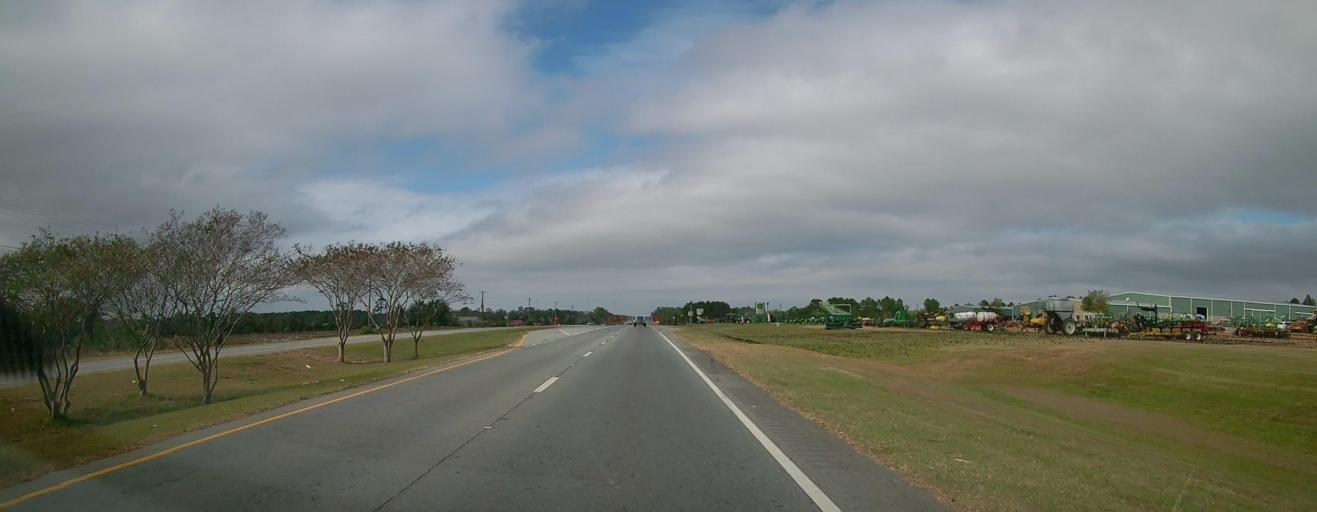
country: US
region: Georgia
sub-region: Colquitt County
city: Moultrie
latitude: 31.1999
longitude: -83.7710
